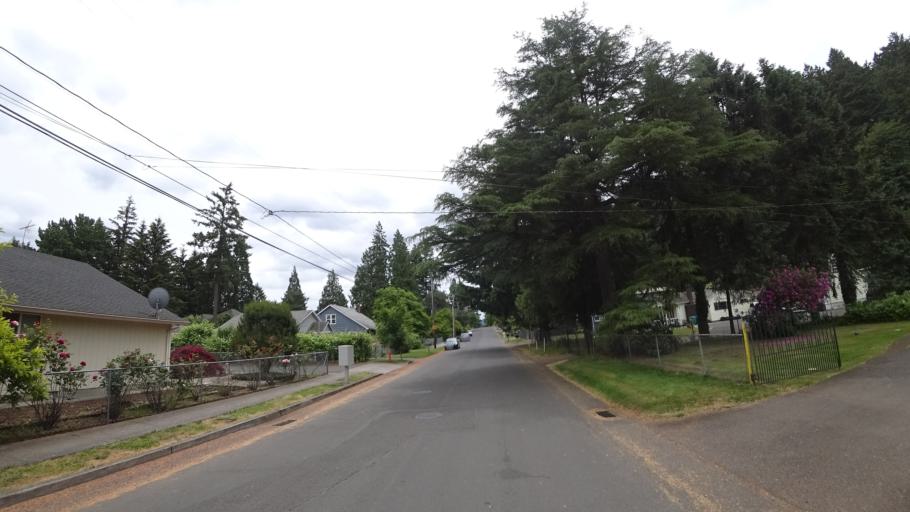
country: US
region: Oregon
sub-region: Multnomah County
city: Lents
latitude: 45.5022
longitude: -122.5514
